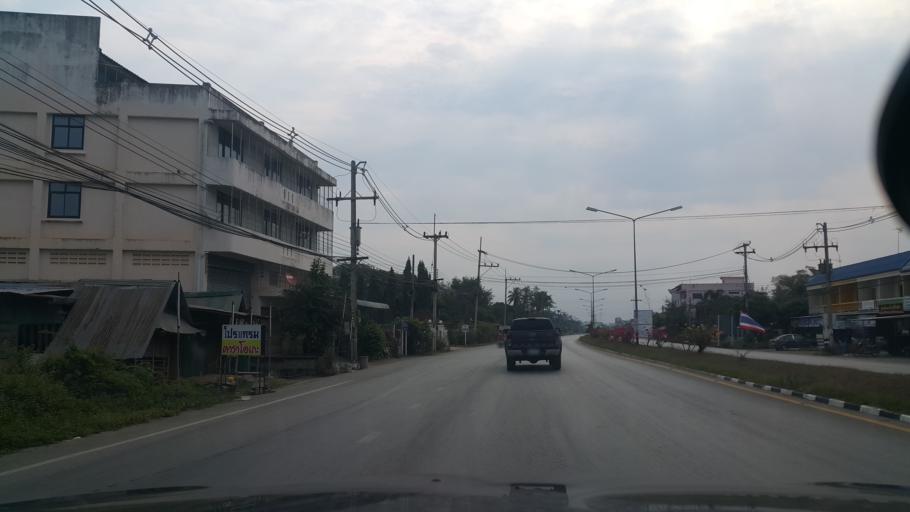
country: TH
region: Sukhothai
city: Si Samrong
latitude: 17.1754
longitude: 99.8520
